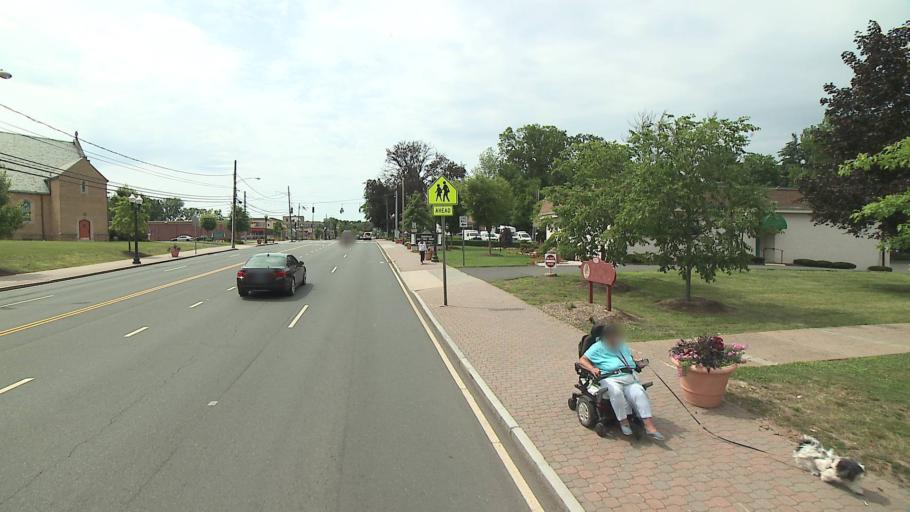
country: US
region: Connecticut
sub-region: Hartford County
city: West Hartford
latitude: 41.7314
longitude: -72.7284
